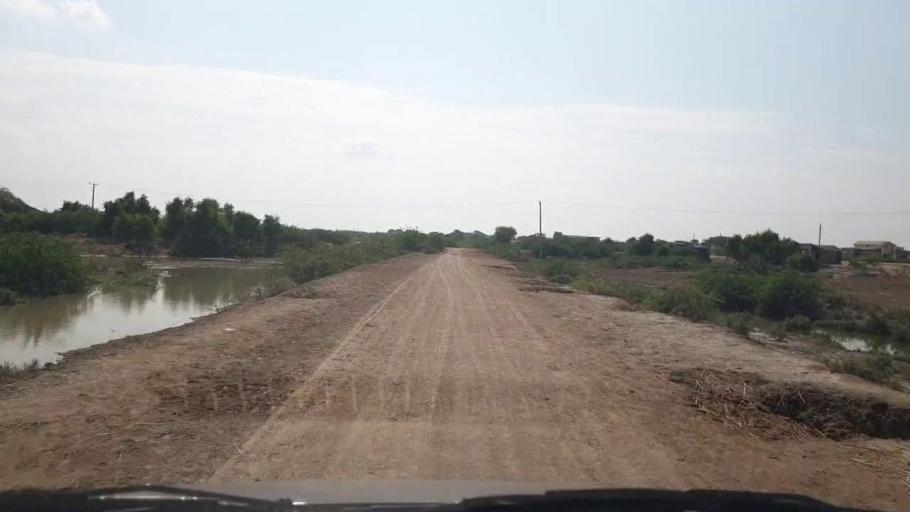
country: PK
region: Sindh
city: Badin
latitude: 24.4802
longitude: 68.6127
